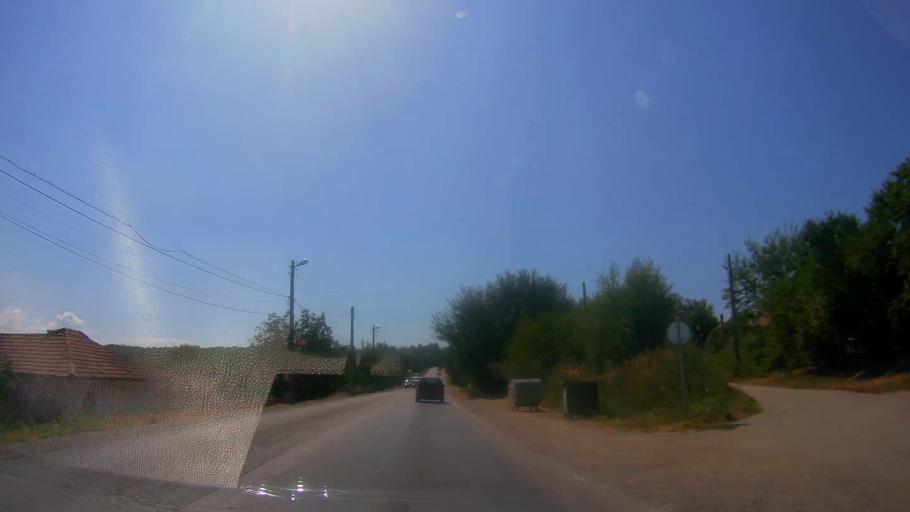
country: BG
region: Veliko Turnovo
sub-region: Obshtina Gorna Oryakhovitsa
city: Purvomaytsi
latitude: 43.1728
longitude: 25.6206
